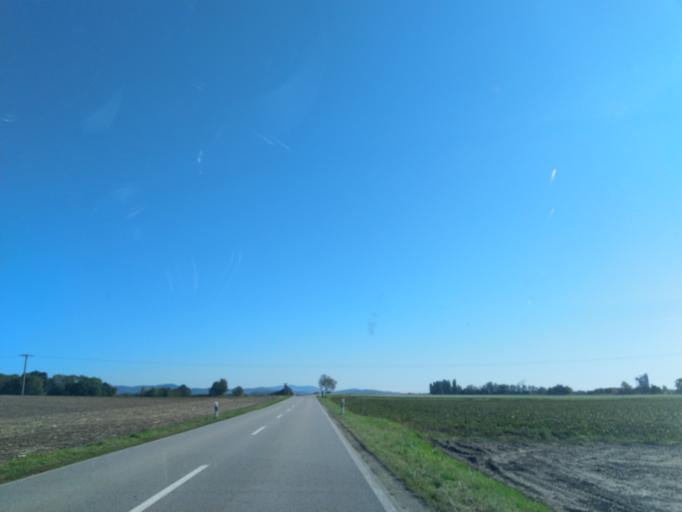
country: DE
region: Bavaria
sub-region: Lower Bavaria
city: Stephansposching
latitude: 48.8242
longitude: 12.8422
